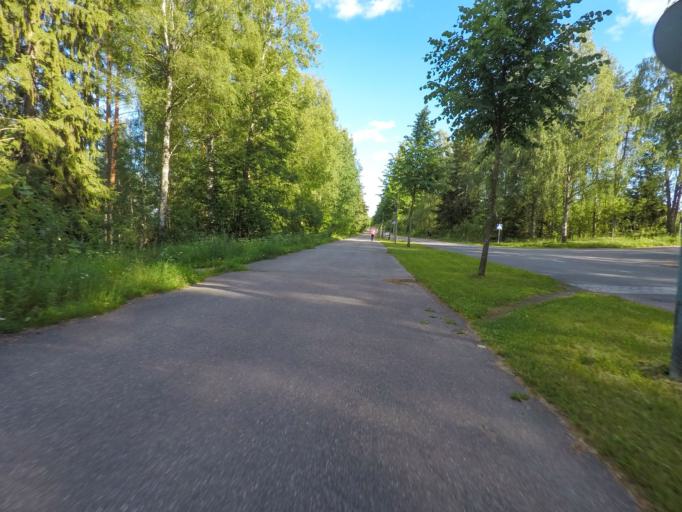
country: FI
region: South Karelia
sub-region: Lappeenranta
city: Lappeenranta
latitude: 61.0726
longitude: 28.1511
